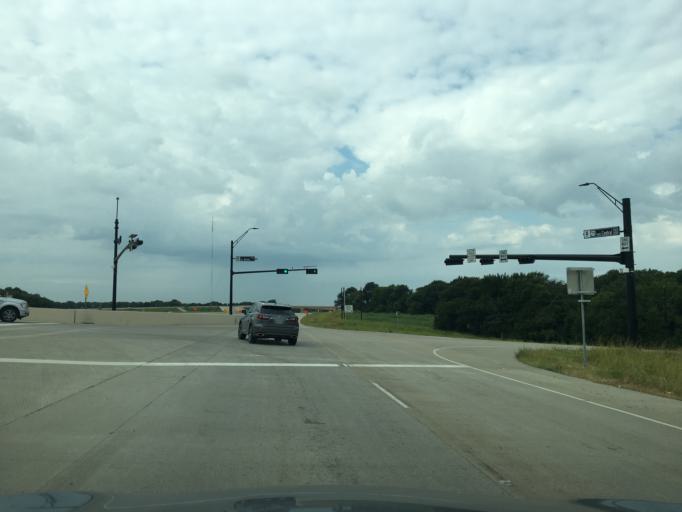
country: US
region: Texas
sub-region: Collin County
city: Melissa
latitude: 33.2702
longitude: -96.5952
